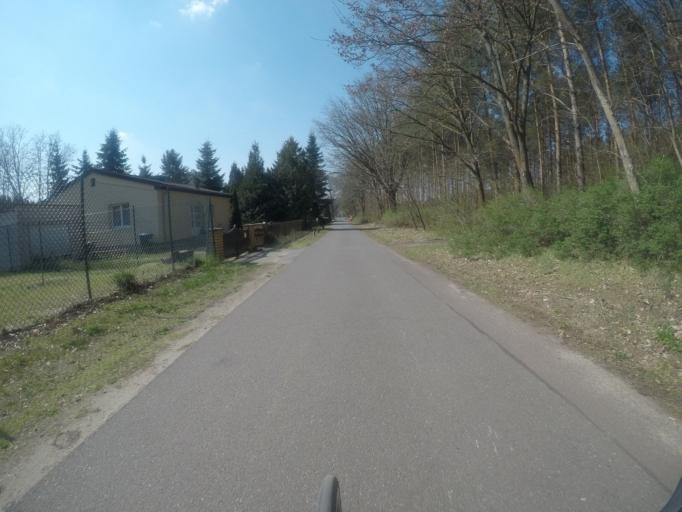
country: DE
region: Brandenburg
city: Falkensee
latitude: 52.6382
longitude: 13.0792
